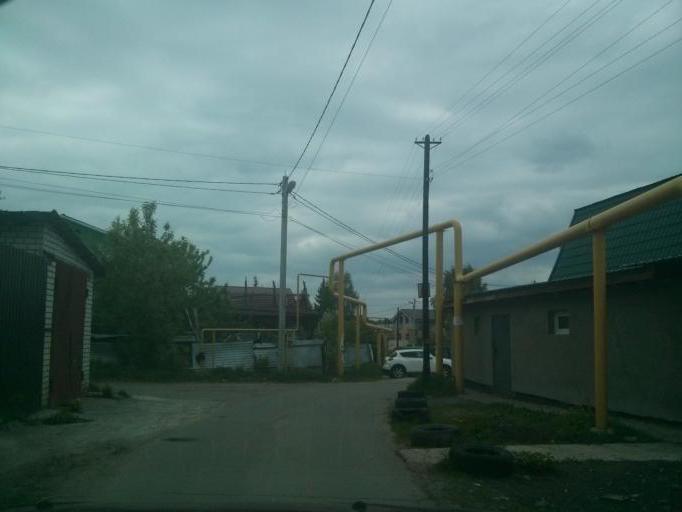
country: RU
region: Nizjnij Novgorod
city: Afonino
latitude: 56.2999
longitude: 44.0997
